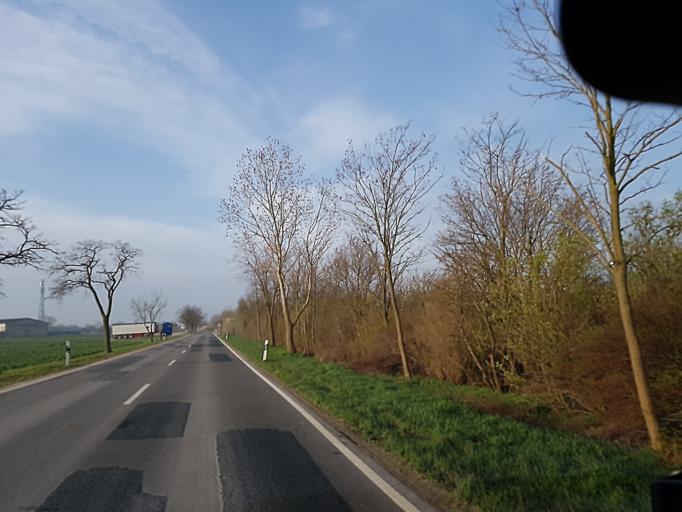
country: DE
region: Brandenburg
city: Muhlberg
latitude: 51.4289
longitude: 13.2678
